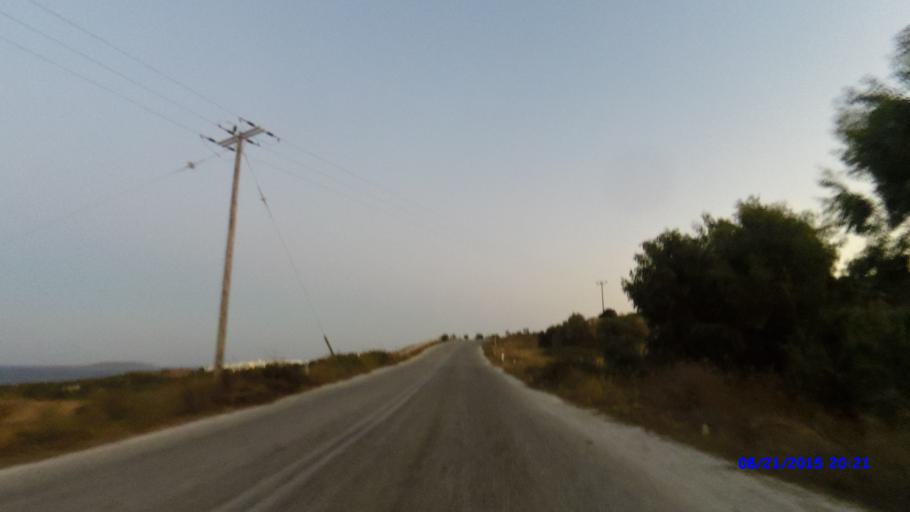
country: GR
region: South Aegean
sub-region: Nomos Kykladon
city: Antiparos
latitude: 36.9982
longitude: 25.0716
